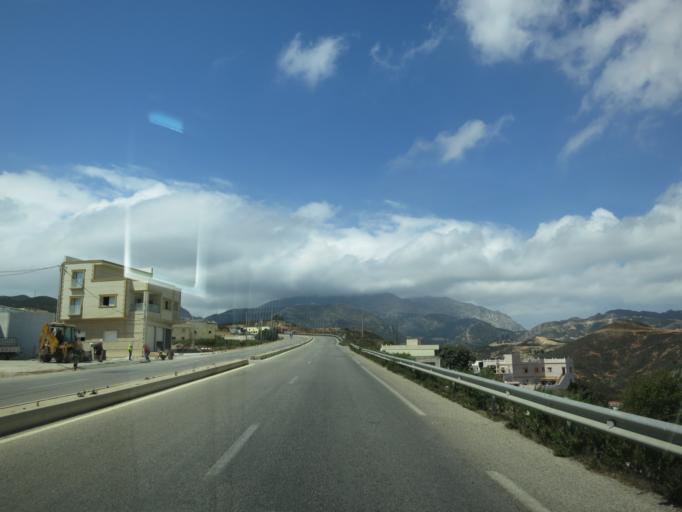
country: ES
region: Ceuta
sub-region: Ceuta
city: Ceuta
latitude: 35.8687
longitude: -5.3604
